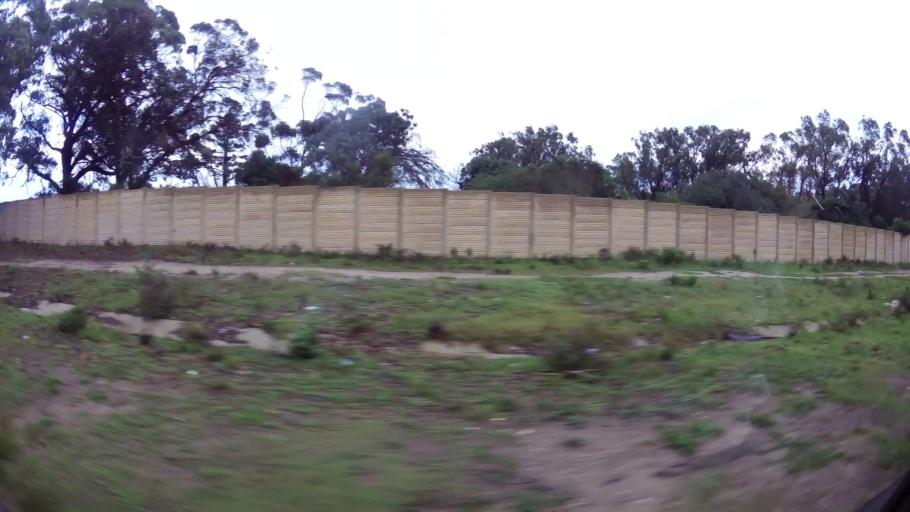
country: ZA
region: Eastern Cape
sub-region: Nelson Mandela Bay Metropolitan Municipality
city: Port Elizabeth
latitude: -33.9929
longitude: 25.5792
